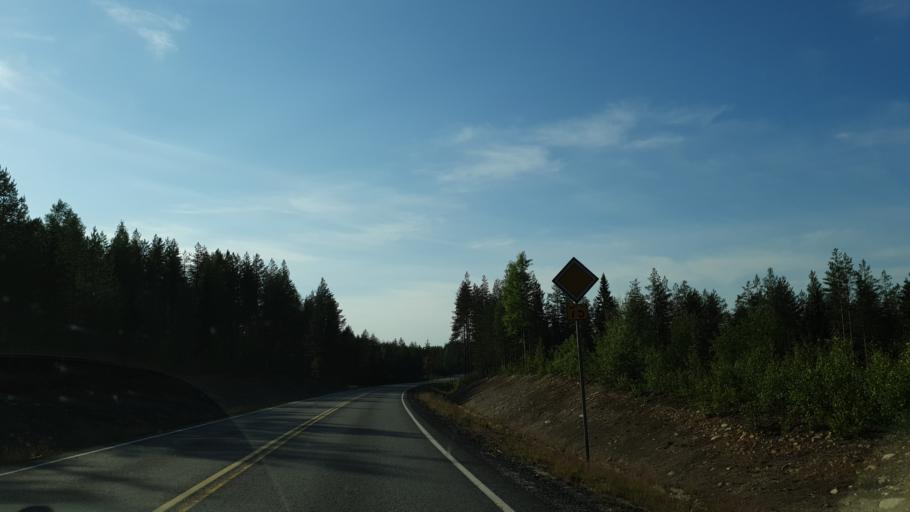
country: FI
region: Kainuu
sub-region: Kehys-Kainuu
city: Kuhmo
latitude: 64.0762
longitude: 29.4909
